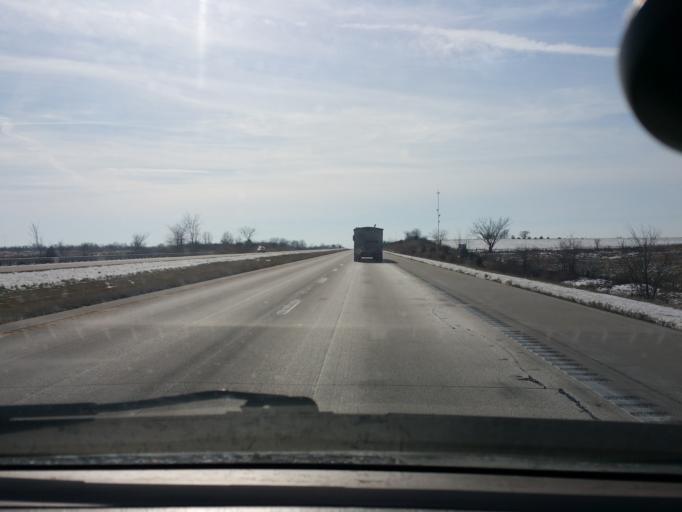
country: US
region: Missouri
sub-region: Clinton County
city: Lathrop
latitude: 39.6213
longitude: -94.2477
